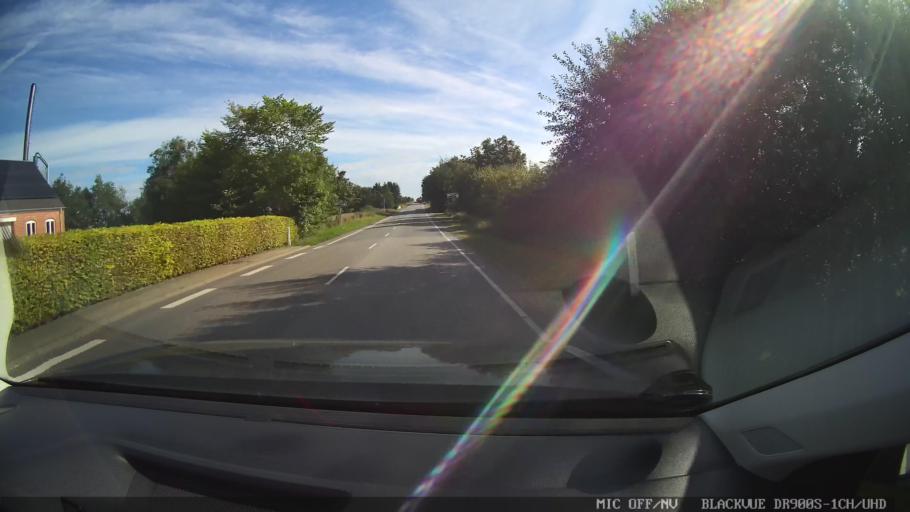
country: DK
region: North Denmark
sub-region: Rebild Kommune
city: Skorping
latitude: 56.7689
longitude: 9.9884
